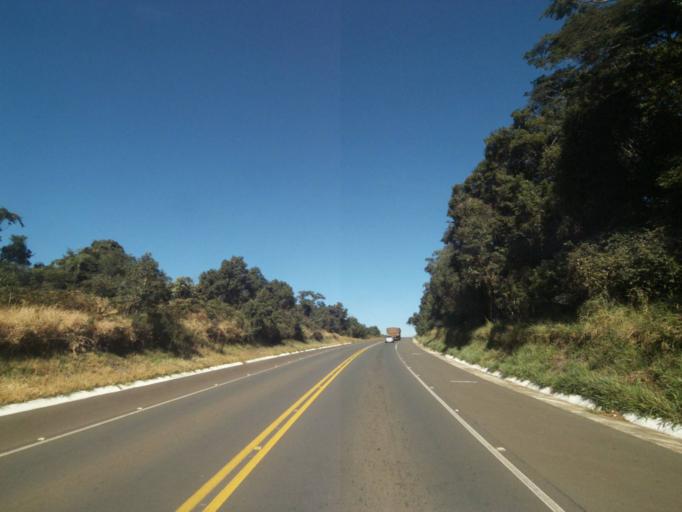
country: BR
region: Parana
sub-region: Tibagi
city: Tibagi
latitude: -24.7156
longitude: -50.4495
